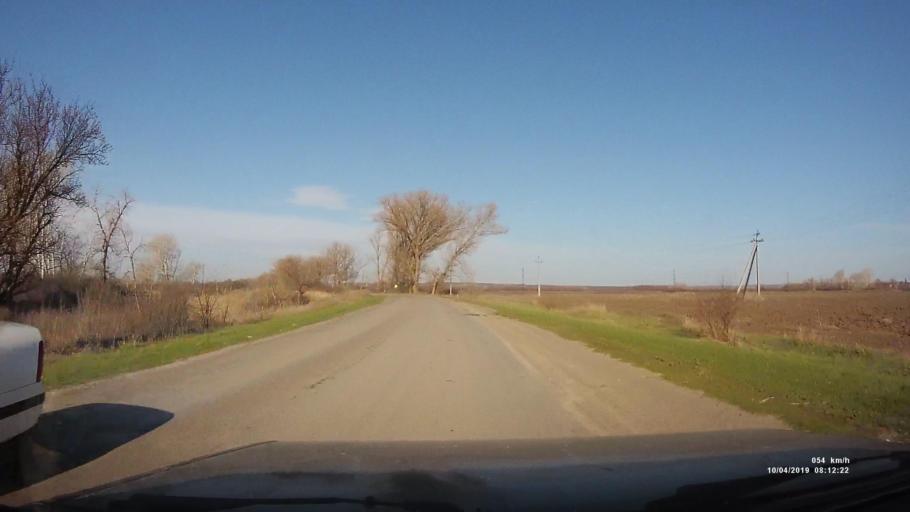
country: RU
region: Rostov
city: Masalovka
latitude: 48.3622
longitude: 40.2583
